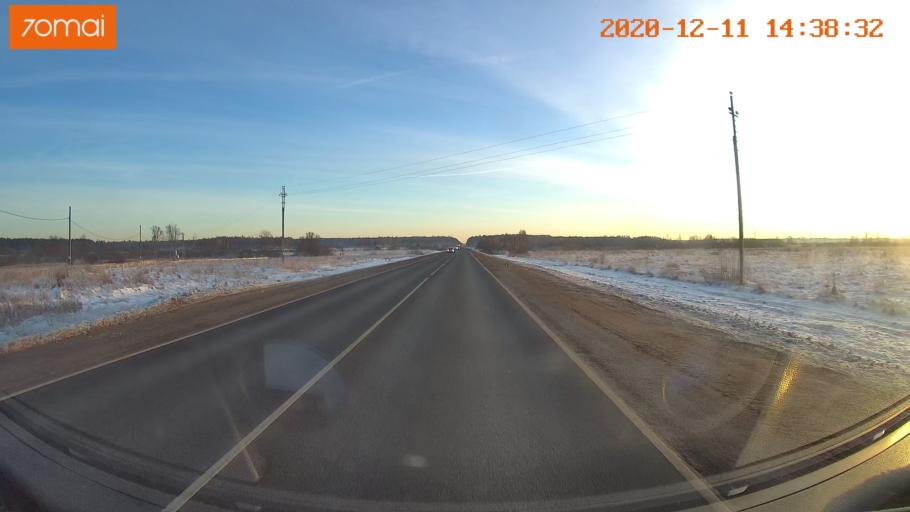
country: RU
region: Kostroma
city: Volgorechensk
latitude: 57.5388
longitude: 41.0148
